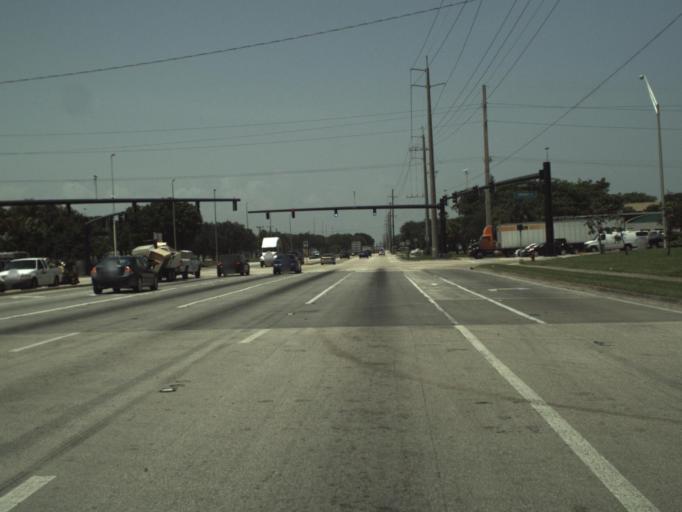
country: US
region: Florida
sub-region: Broward County
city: Coconut Creek
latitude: 26.2594
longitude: -80.1517
